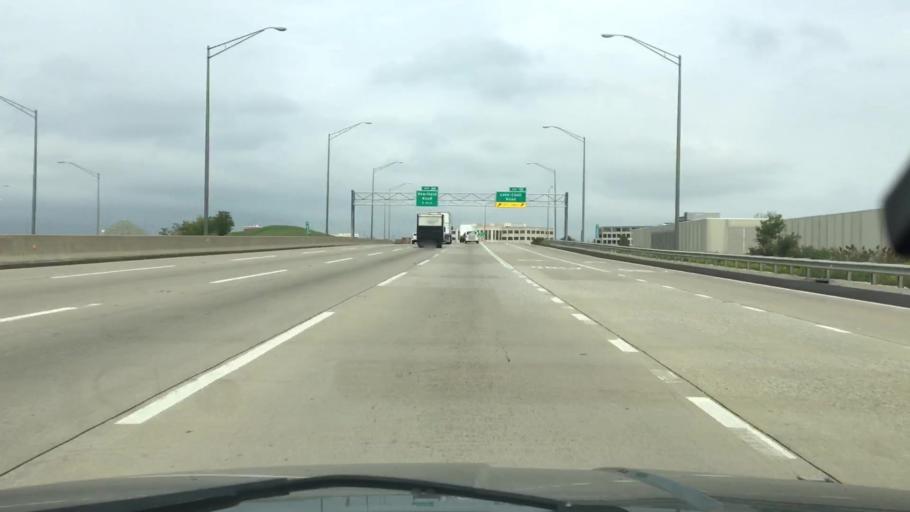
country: US
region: Illinois
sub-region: Lake County
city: Riverwoods
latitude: 42.1489
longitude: -87.8760
